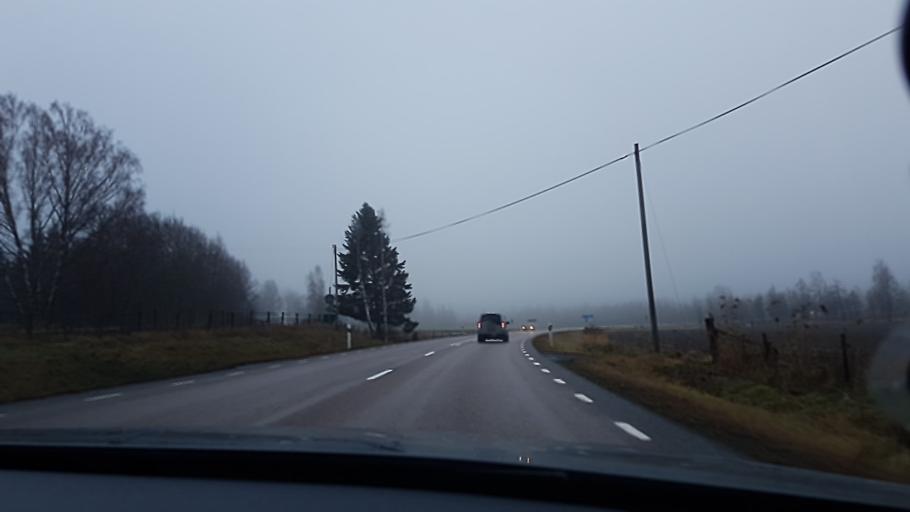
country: SE
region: Vaestra Goetaland
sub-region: Gullspangs Kommun
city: Gullspang
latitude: 58.9944
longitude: 14.1016
